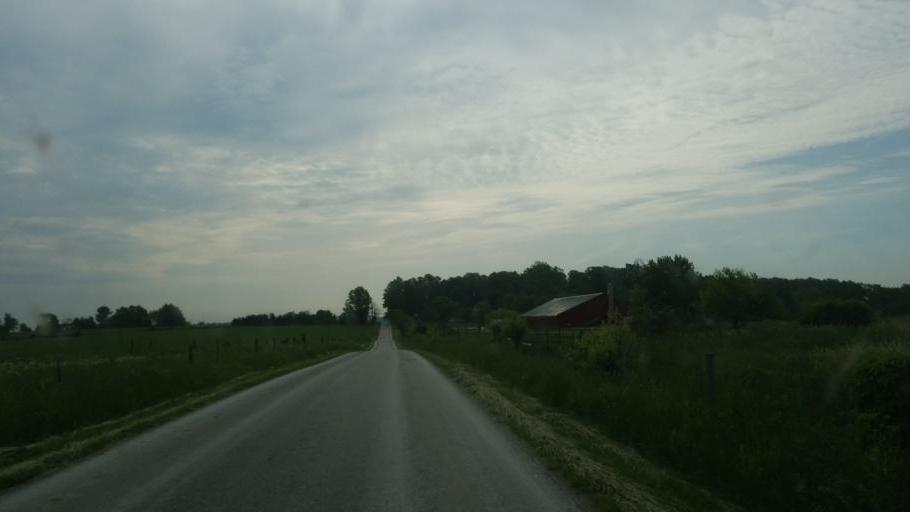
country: US
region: Ohio
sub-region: Wayne County
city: Apple Creek
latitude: 40.6824
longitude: -81.7606
